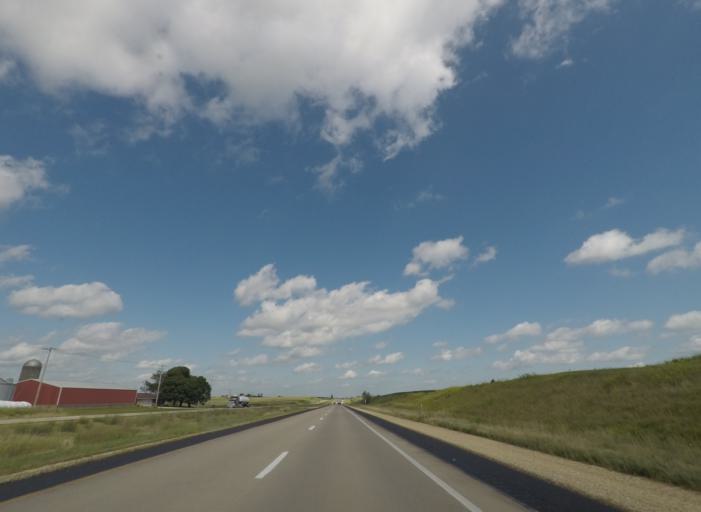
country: US
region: Iowa
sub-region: Dubuque County
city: Cascade
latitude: 42.2918
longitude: -91.0643
